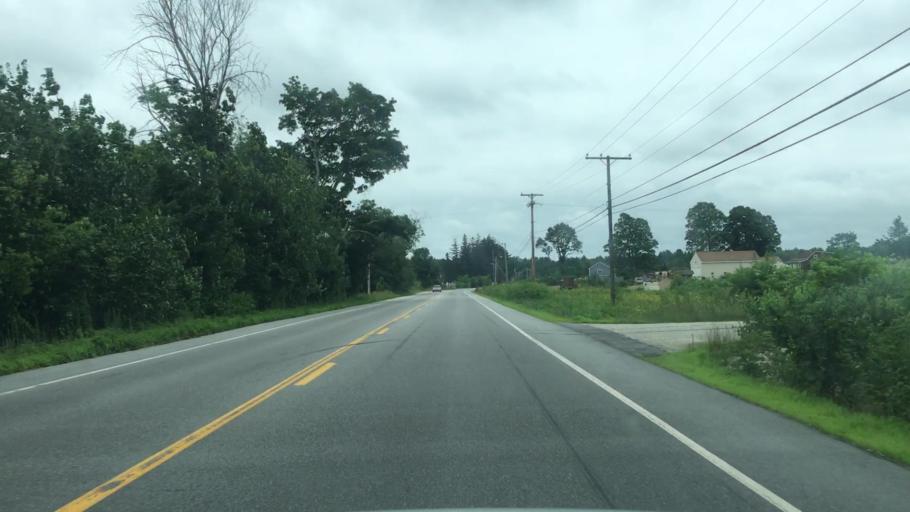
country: US
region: Maine
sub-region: York County
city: Biddeford
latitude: 43.5210
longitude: -70.4856
